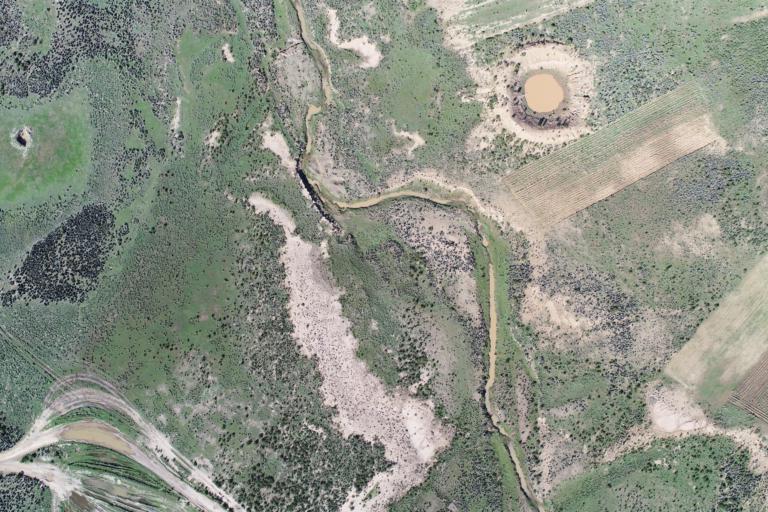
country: BO
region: La Paz
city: Curahuara de Carangas
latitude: -17.3036
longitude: -68.5231
